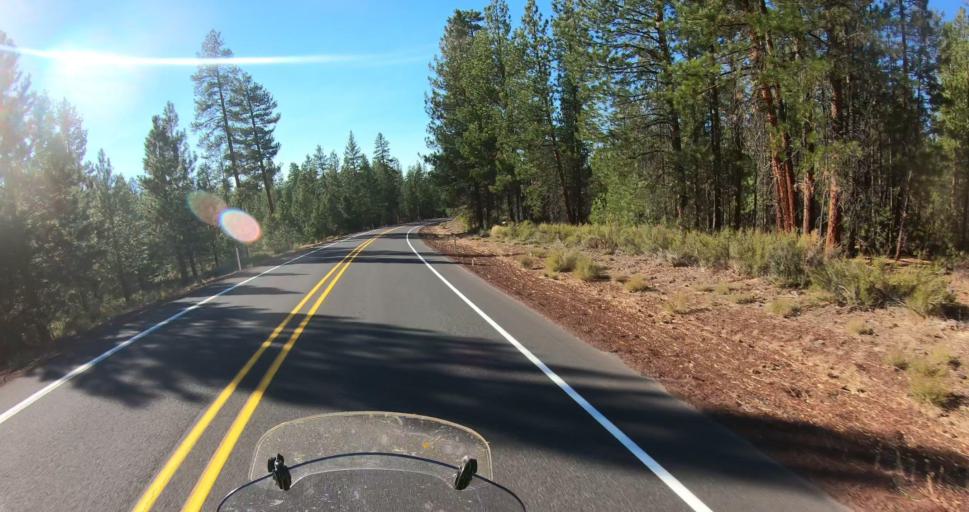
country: US
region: Oregon
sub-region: Deschutes County
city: La Pine
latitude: 43.4680
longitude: -121.3952
